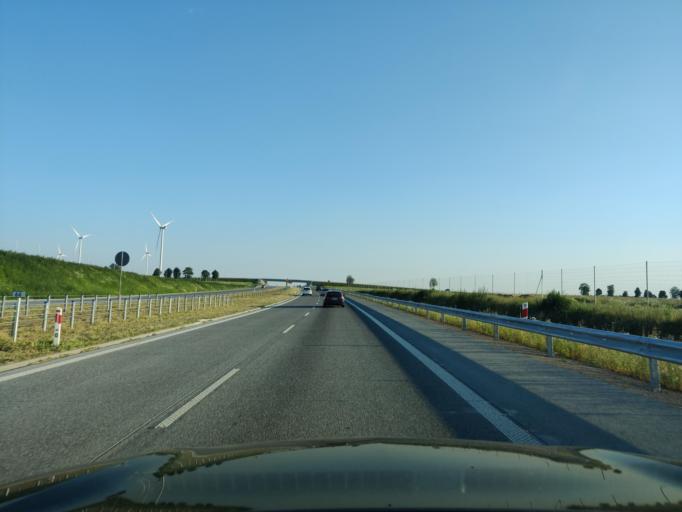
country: PL
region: Masovian Voivodeship
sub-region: Powiat mlawski
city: Wisniewo
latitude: 53.0660
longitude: 20.3679
